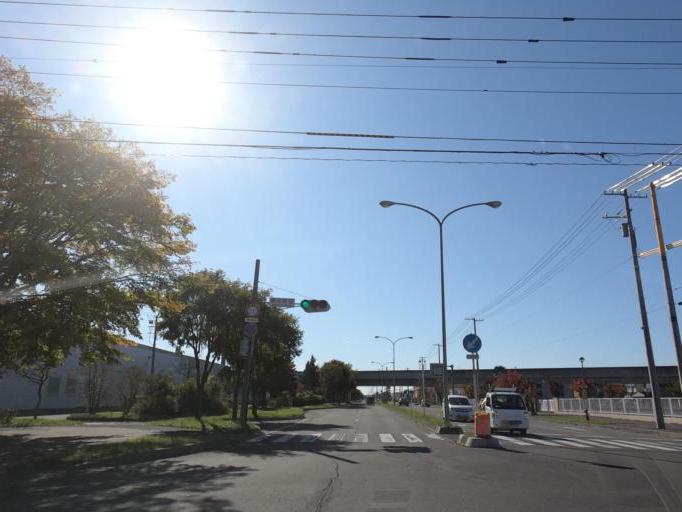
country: JP
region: Hokkaido
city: Obihiro
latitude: 42.9150
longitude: 143.2132
